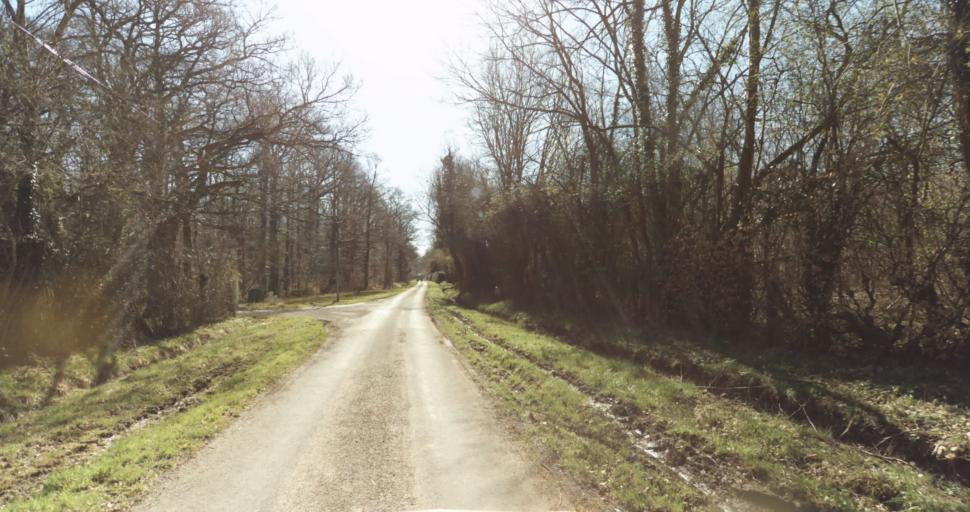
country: FR
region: Lower Normandy
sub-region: Departement du Calvados
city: Livarot
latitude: 48.9614
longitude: 0.0817
